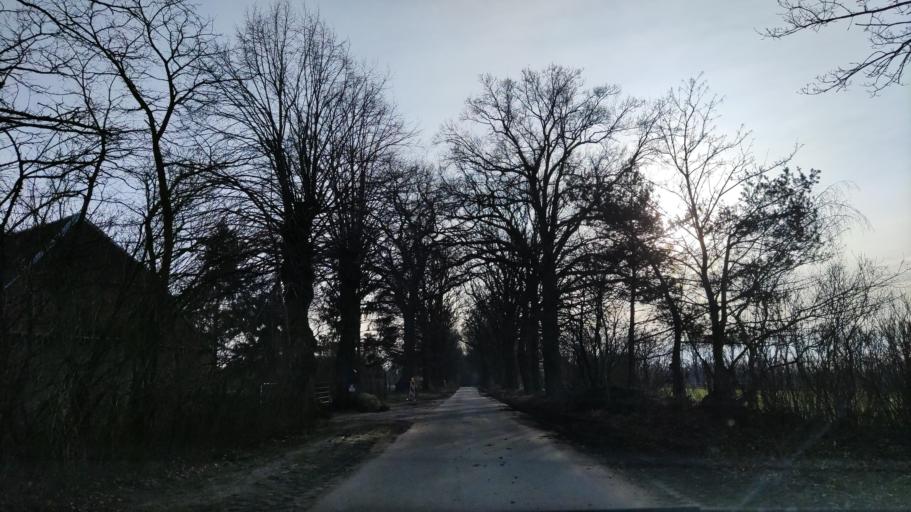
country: DE
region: Schleswig-Holstein
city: Langenlehsten
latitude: 53.4646
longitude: 10.7769
